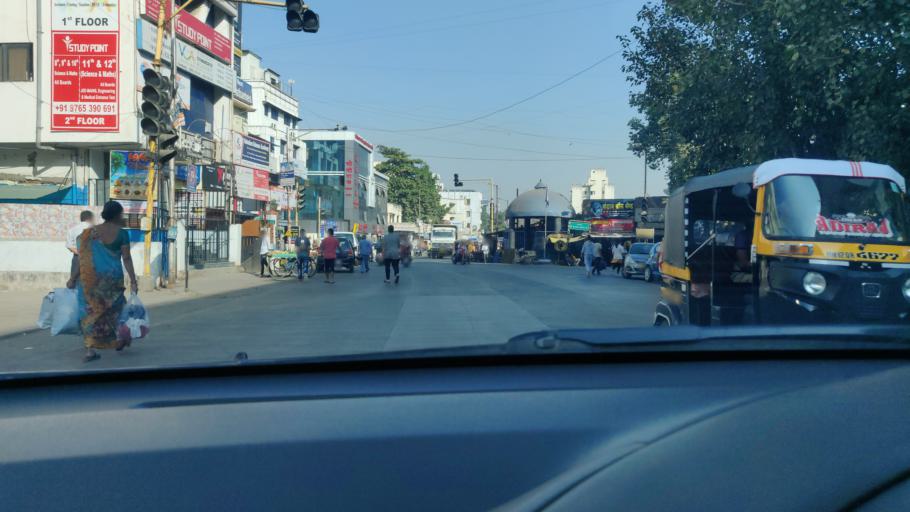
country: IN
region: Maharashtra
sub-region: Pune Division
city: Khadki
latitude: 18.5600
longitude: 73.8032
